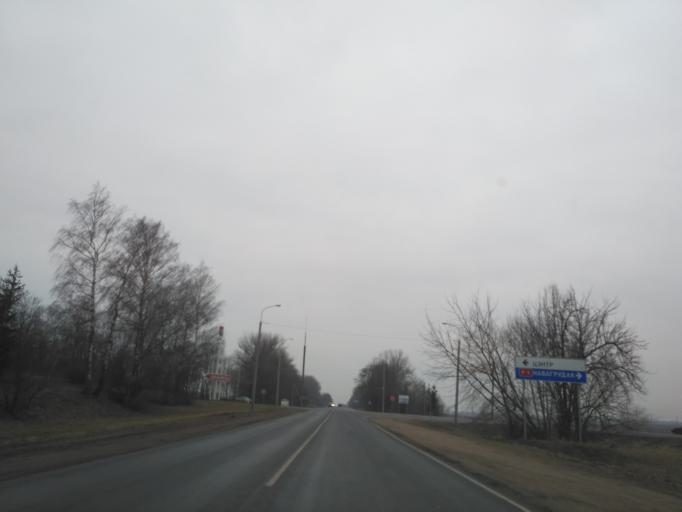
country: BY
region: Brest
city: Baranovichi
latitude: 53.1670
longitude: 26.0280
